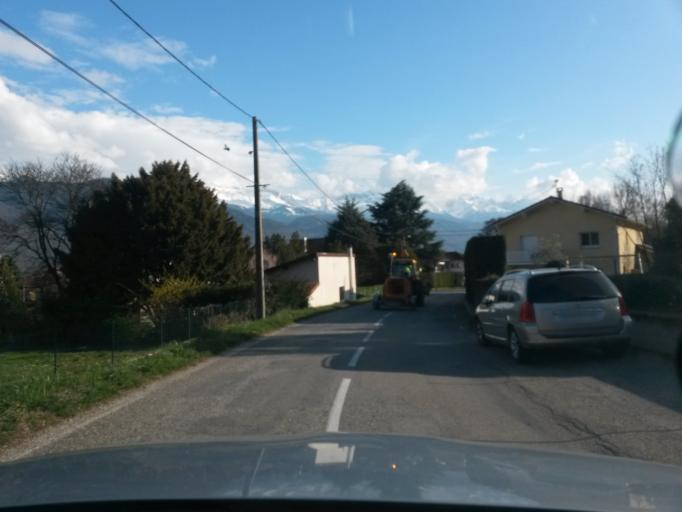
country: FR
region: Rhone-Alpes
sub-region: Departement de l'Isere
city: Le Touvet
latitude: 45.3582
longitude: 5.9485
